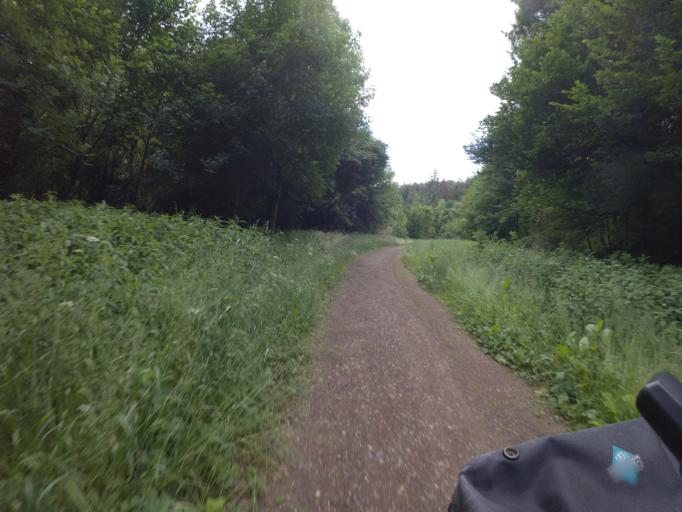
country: DE
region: Rheinland-Pfalz
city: Schweisweiler
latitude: 49.5871
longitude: 7.8369
